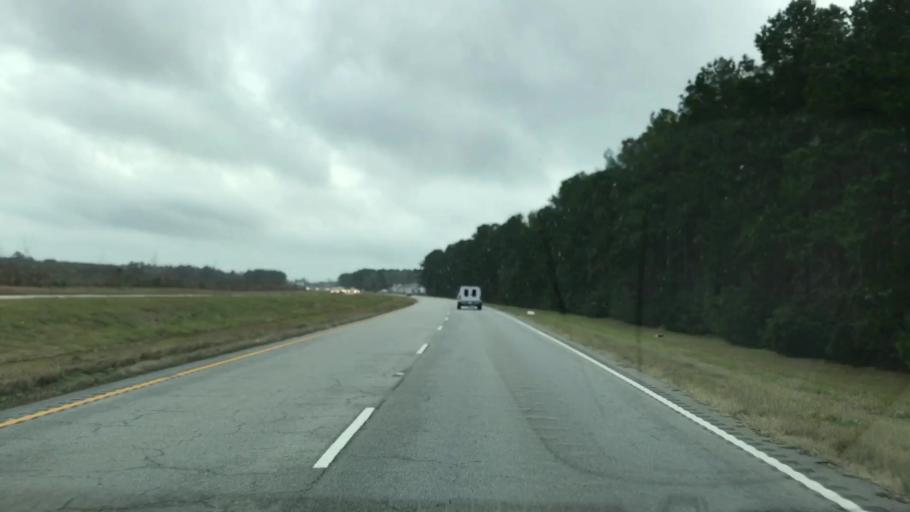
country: US
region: South Carolina
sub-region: Berkeley County
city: Moncks Corner
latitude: 33.1580
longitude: -80.0326
